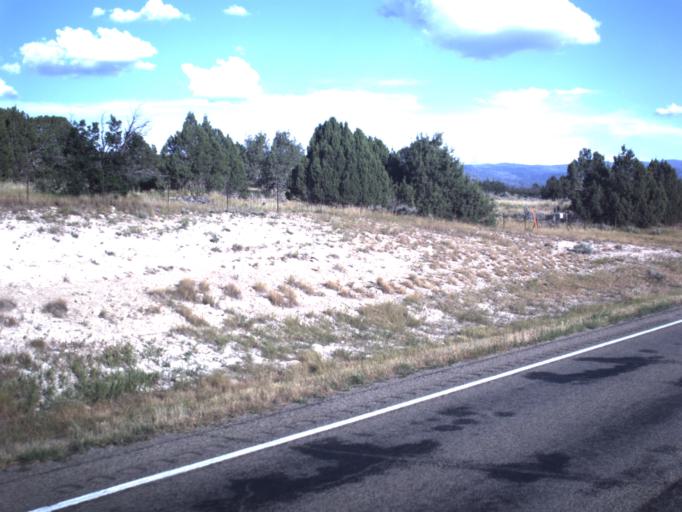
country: US
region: Utah
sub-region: Sanpete County
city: Fairview
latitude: 39.6831
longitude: -111.4584
